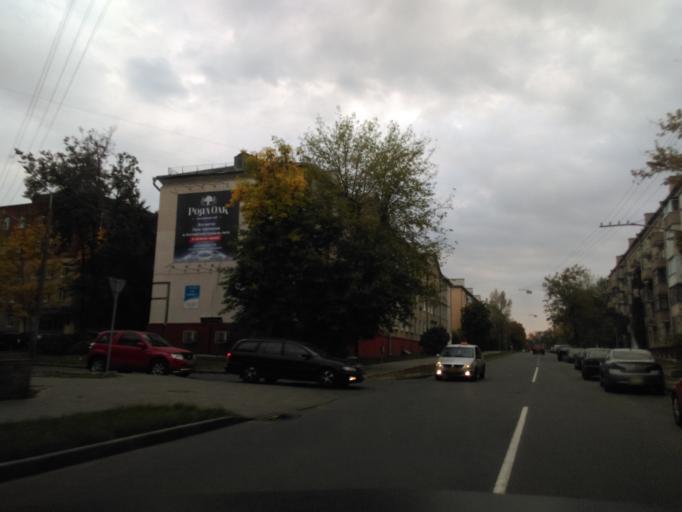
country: BY
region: Minsk
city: Minsk
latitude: 53.9128
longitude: 27.5857
